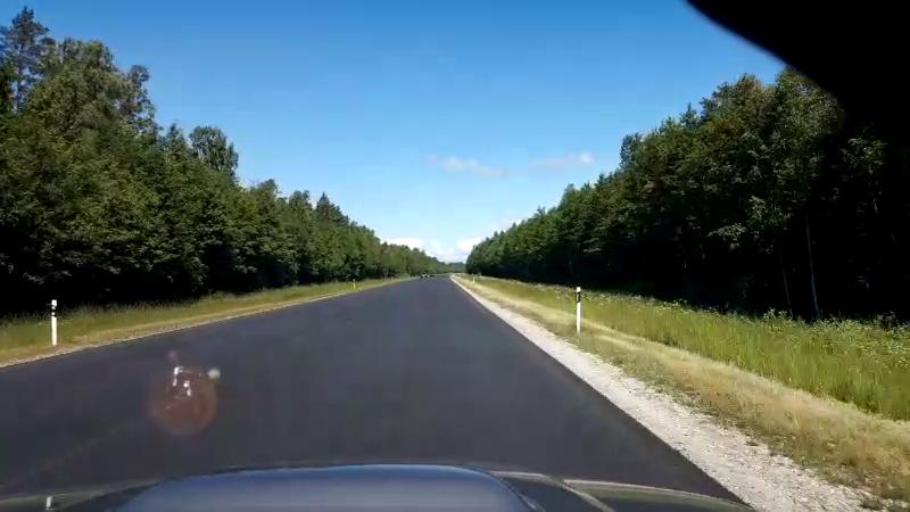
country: LV
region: Salacgrivas
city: Ainazi
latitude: 57.9317
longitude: 24.4270
